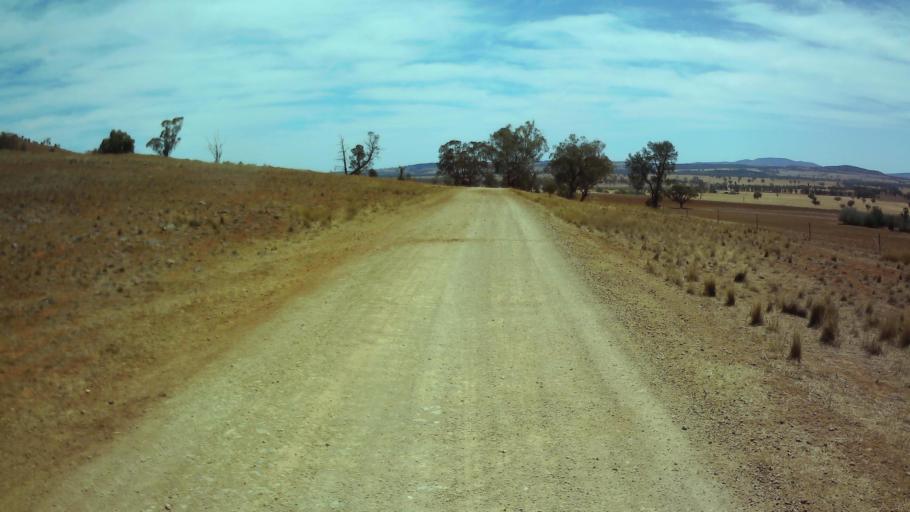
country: AU
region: New South Wales
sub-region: Weddin
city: Grenfell
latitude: -33.7478
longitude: 148.1678
